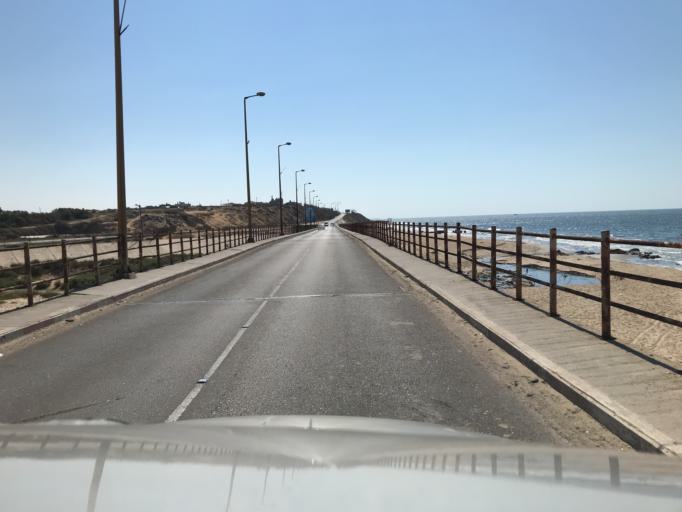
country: PS
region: Gaza Strip
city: An Nusayrat
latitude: 31.4643
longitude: 34.3766
